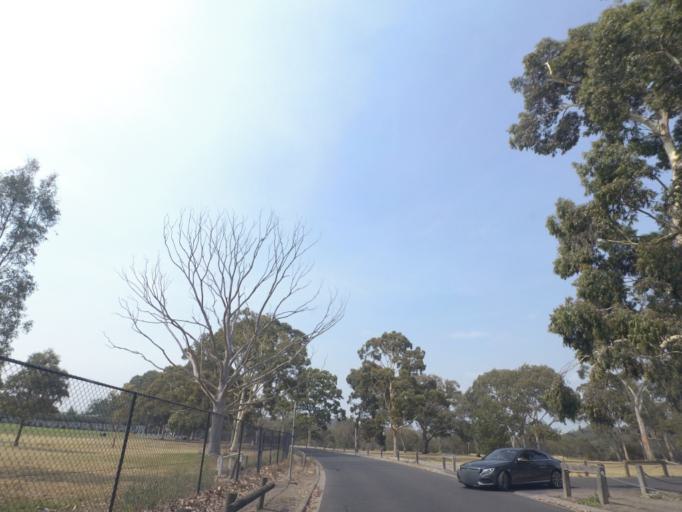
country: AU
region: Victoria
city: Abbotsford
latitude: -37.7949
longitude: 145.0099
